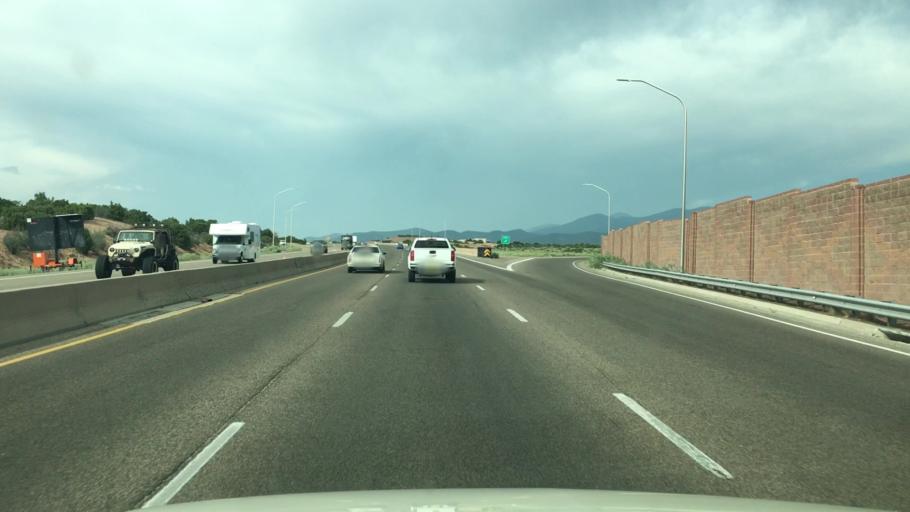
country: US
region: New Mexico
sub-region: Santa Fe County
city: Santa Fe
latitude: 35.7069
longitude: -105.9429
